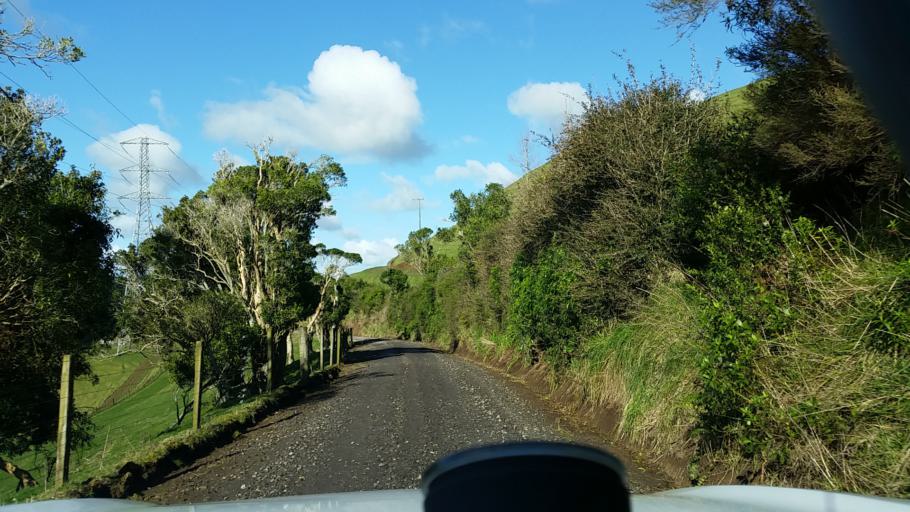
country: NZ
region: Taranaki
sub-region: South Taranaki District
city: Eltham
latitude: -39.4544
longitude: 174.3686
